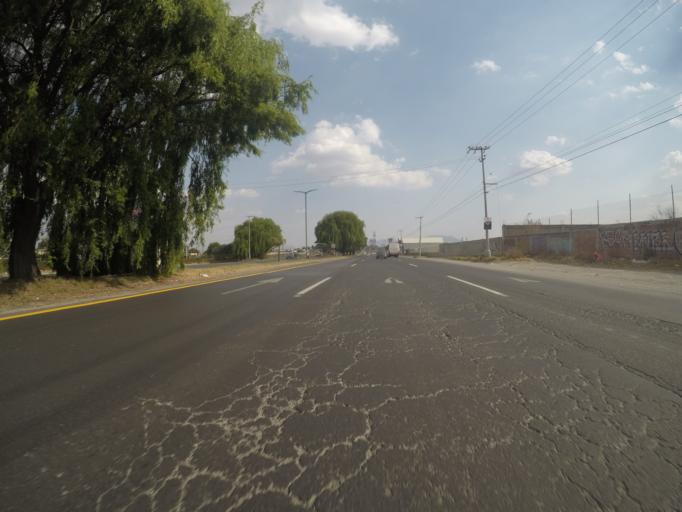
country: MX
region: Morelos
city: San Miguel Totocuitlapilco
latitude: 19.2203
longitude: -99.5924
